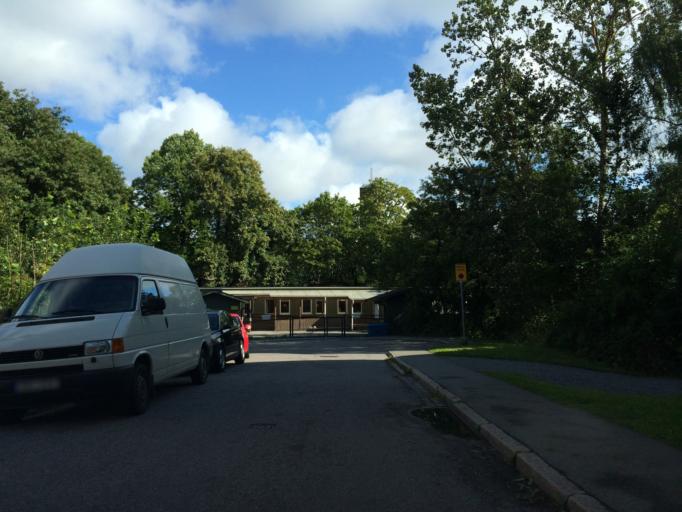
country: SE
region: Stockholm
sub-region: Stockholms Kommun
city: Arsta
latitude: 59.3024
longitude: 18.0043
